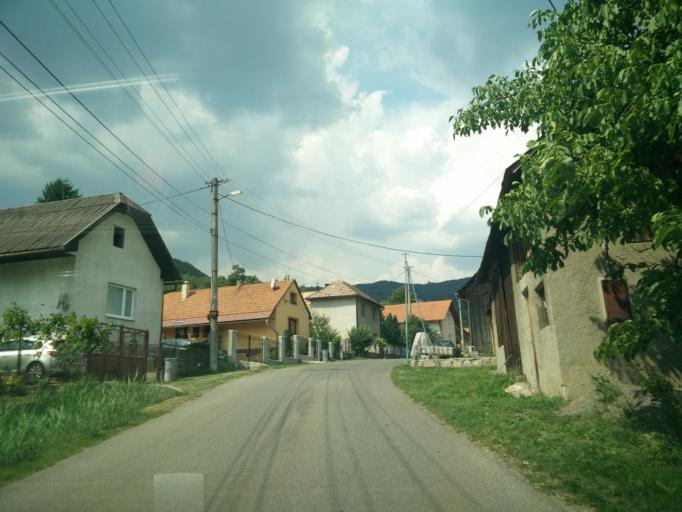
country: SK
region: Nitriansky
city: Handlova
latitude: 48.6158
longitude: 18.7052
